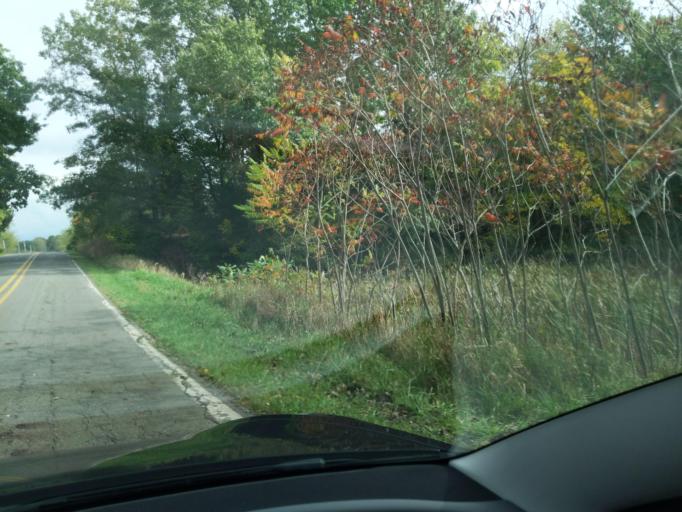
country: US
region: Michigan
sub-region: Ingham County
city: Leslie
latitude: 42.4114
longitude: -84.4768
